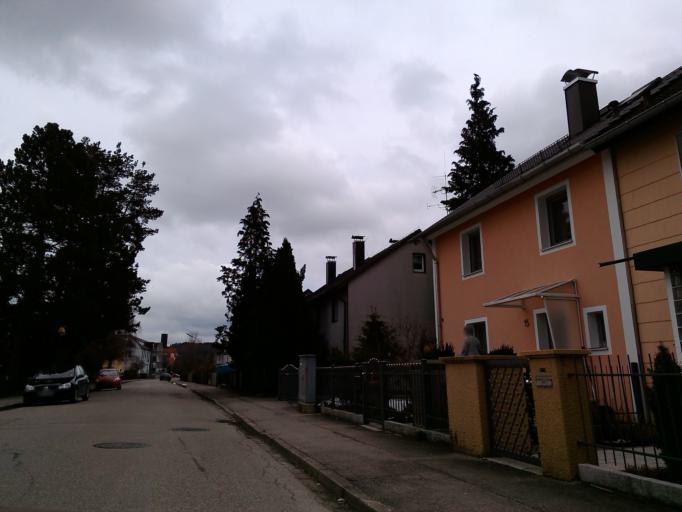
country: DE
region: Bavaria
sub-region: Upper Bavaria
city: Gilching
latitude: 48.1046
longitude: 11.2893
